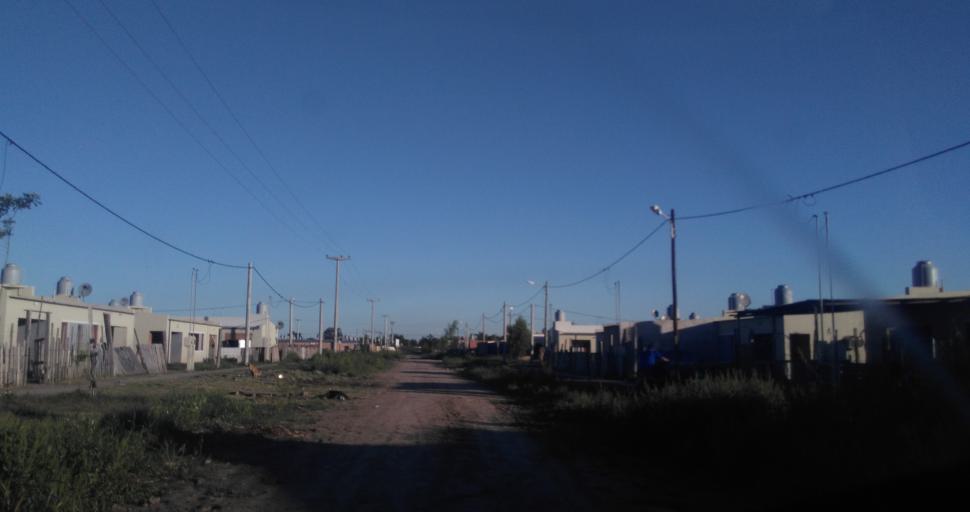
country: AR
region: Chaco
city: Fontana
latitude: -27.3962
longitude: -58.9893
